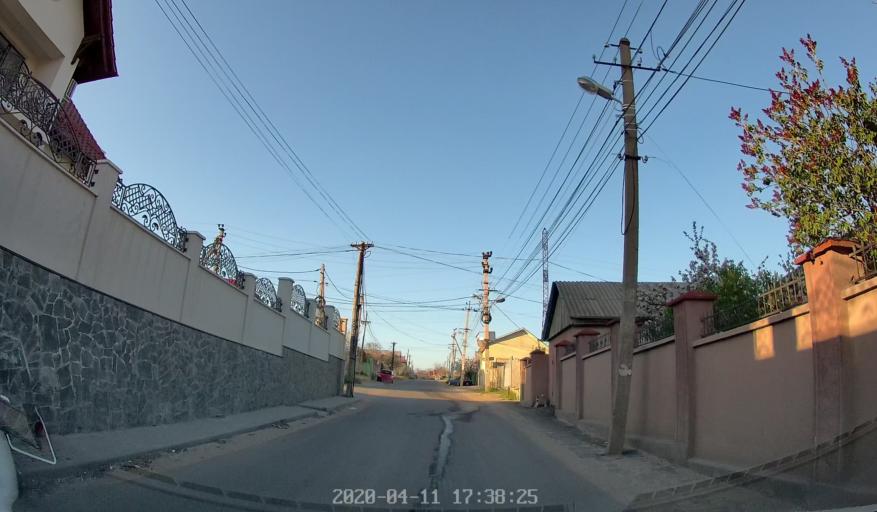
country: MD
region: Laloveni
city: Ialoveni
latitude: 46.9827
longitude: 28.8033
